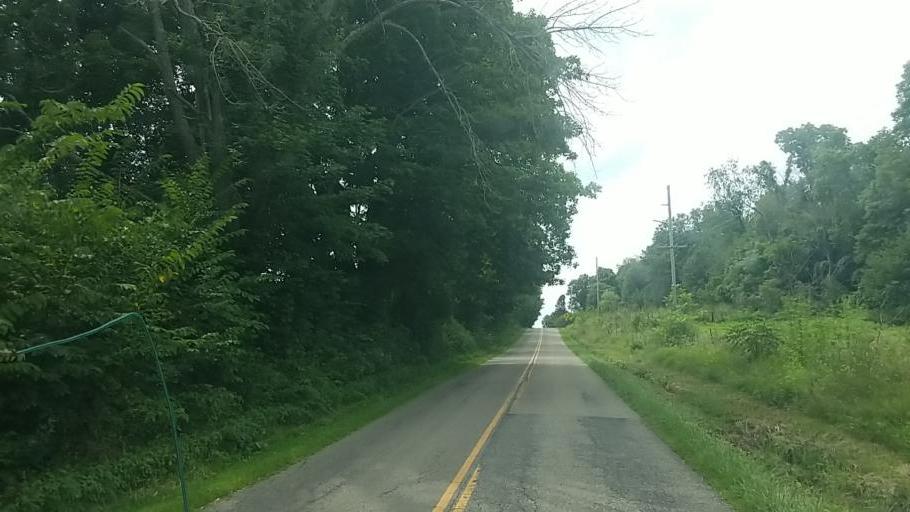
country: US
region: Ohio
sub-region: Knox County
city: Gambier
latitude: 40.3155
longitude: -82.3797
